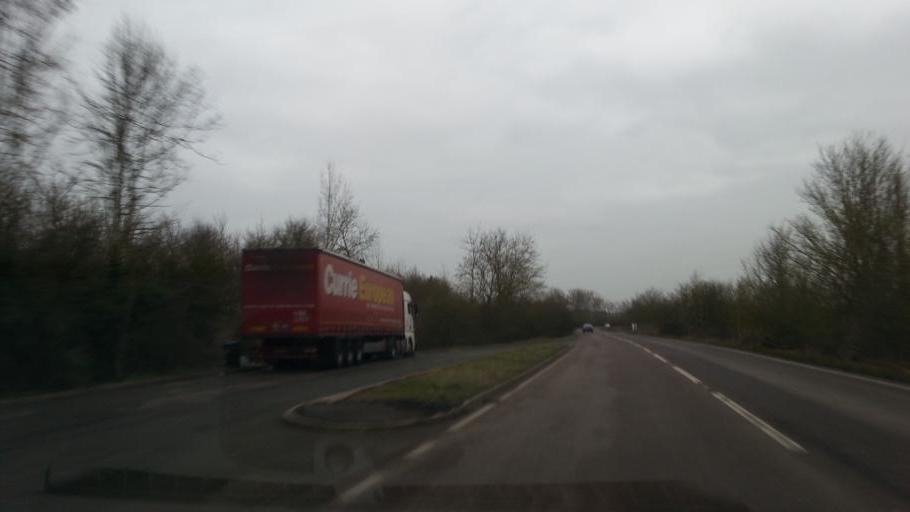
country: GB
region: England
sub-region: Central Bedfordshire
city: Lidlington
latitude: 52.0512
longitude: -0.5728
